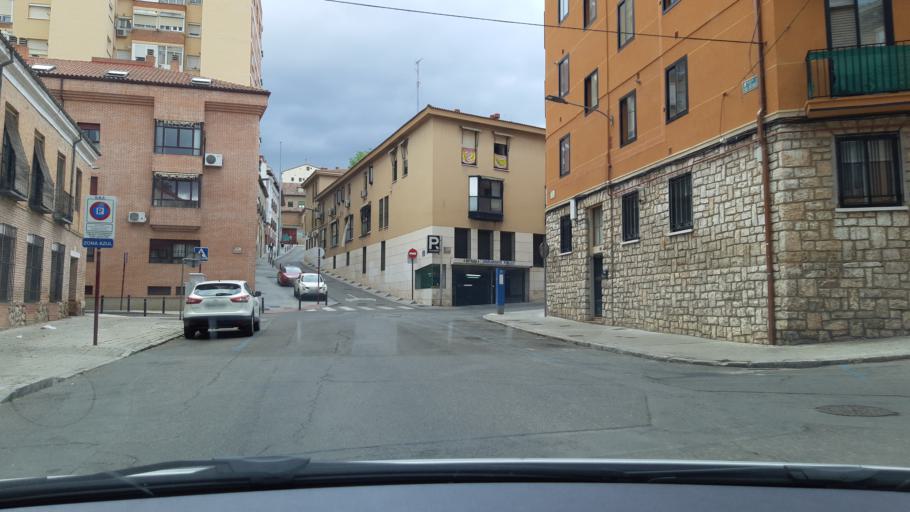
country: ES
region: Castille-La Mancha
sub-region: Provincia de Guadalajara
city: Guadalajara
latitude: 40.6340
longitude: -3.1698
